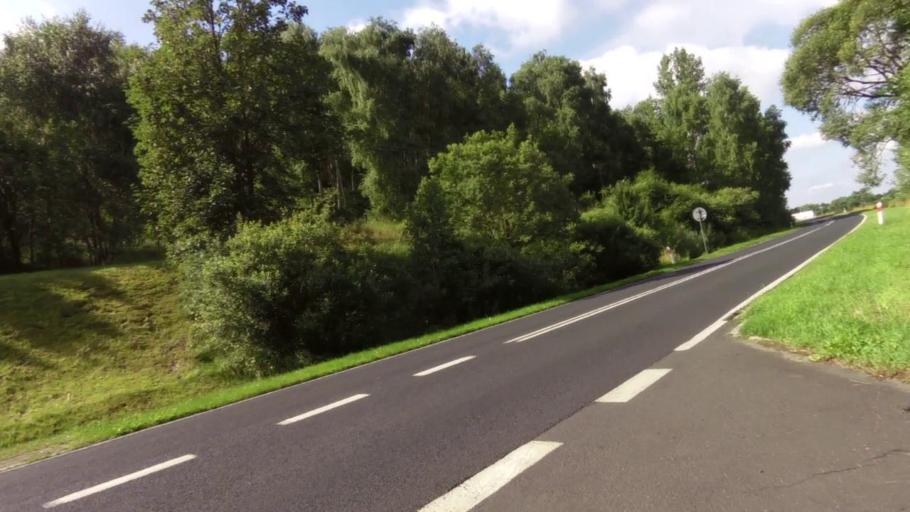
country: PL
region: West Pomeranian Voivodeship
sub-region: Powiat gryfinski
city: Cedynia
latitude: 52.8559
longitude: 14.1558
